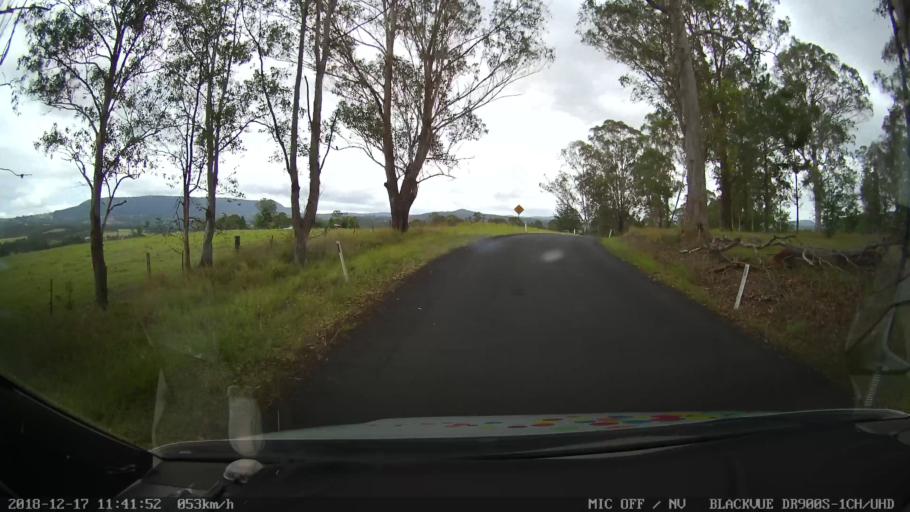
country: AU
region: New South Wales
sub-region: Kyogle
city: Kyogle
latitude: -28.6713
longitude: 152.5879
